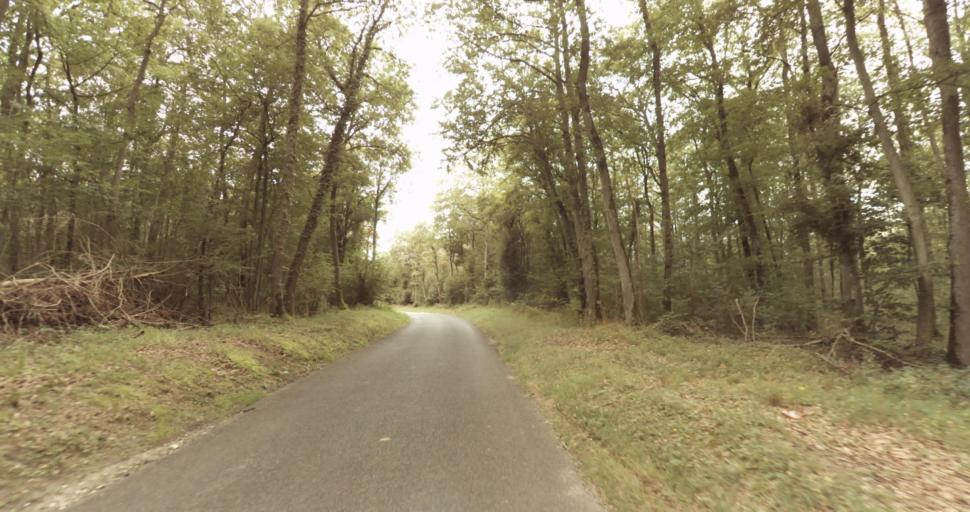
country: FR
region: Haute-Normandie
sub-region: Departement de l'Eure
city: Menilles
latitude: 49.0320
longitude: 1.3114
